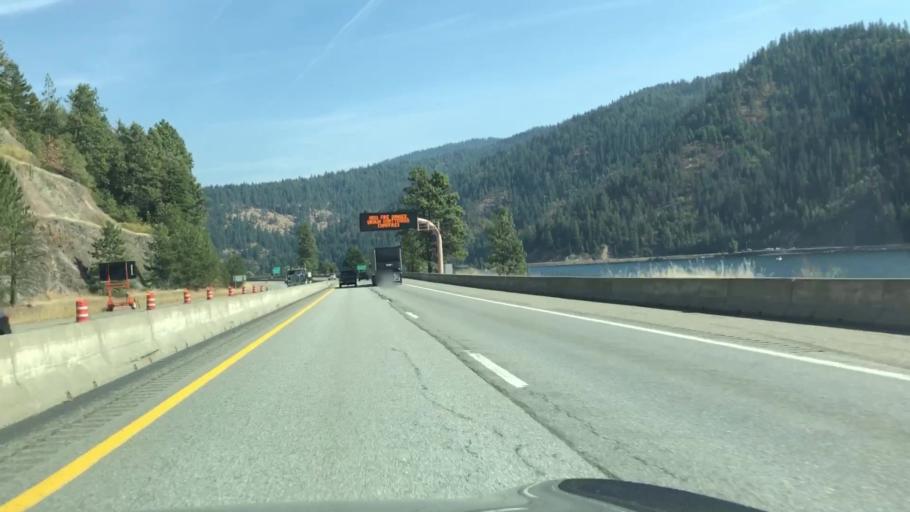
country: US
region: Idaho
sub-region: Kootenai County
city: Coeur d'Alene
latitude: 47.6248
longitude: -116.6685
